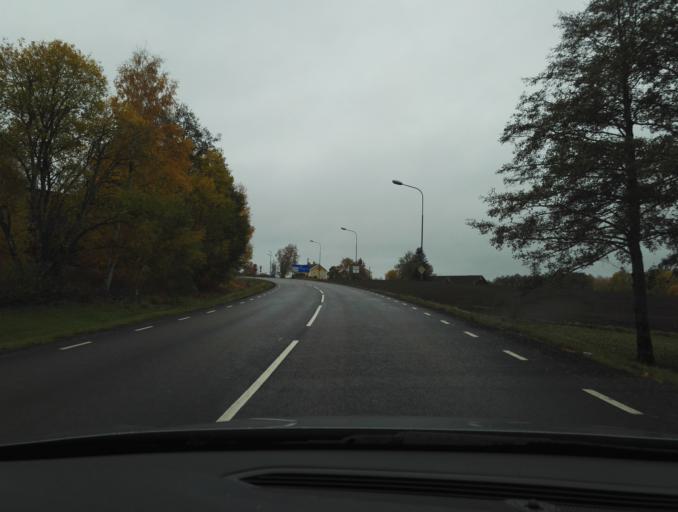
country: SE
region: Kronoberg
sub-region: Vaxjo Kommun
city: Rottne
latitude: 57.0254
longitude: 14.8857
